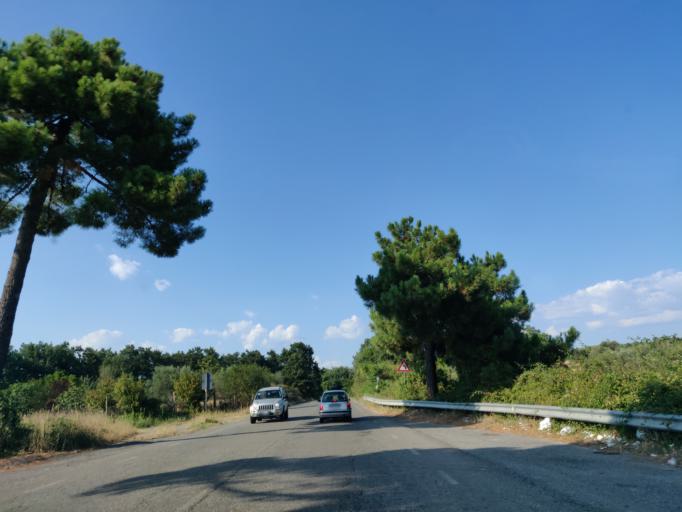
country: IT
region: Latium
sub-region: Provincia di Viterbo
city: Valentano
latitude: 42.5902
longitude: 11.8367
